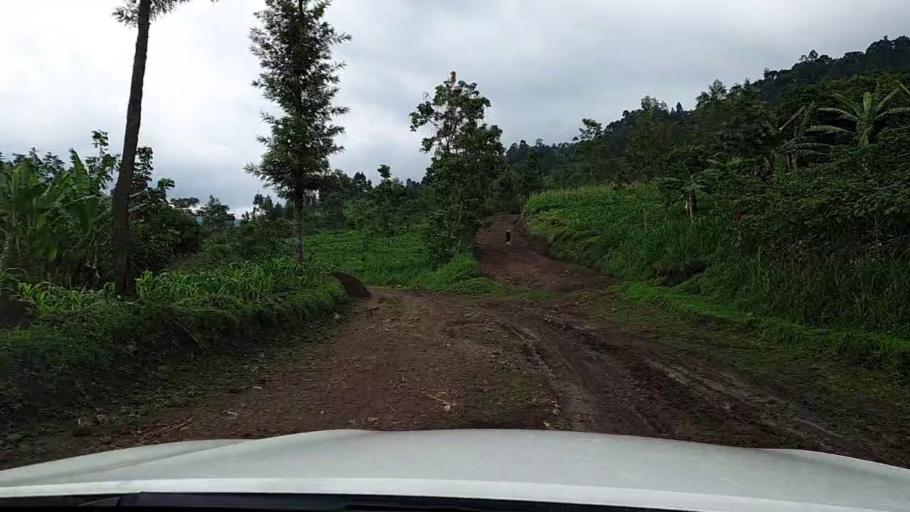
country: RW
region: Western Province
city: Cyangugu
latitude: -2.5613
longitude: 29.0360
